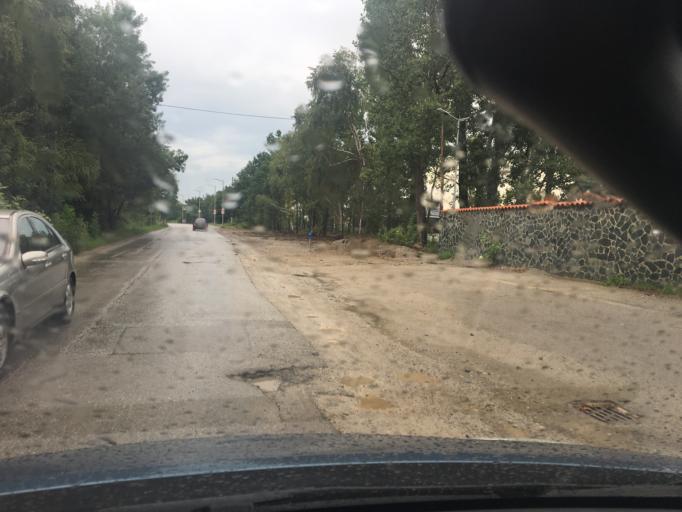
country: BG
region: Sofia-Capital
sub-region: Stolichna Obshtina
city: Sofia
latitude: 42.6402
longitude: 23.2948
